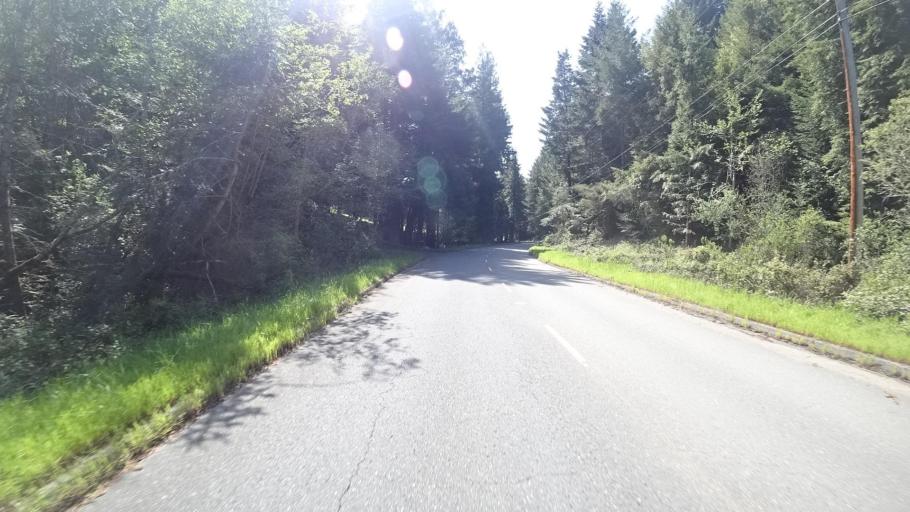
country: US
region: California
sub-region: Humboldt County
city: Hydesville
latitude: 40.5692
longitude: -124.1112
